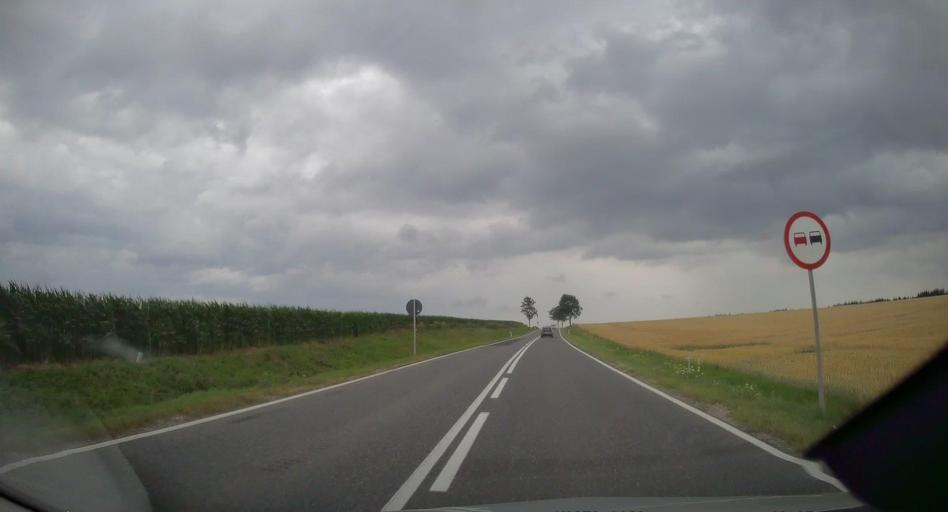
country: PL
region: Opole Voivodeship
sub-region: Powiat prudnicki
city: Moszczanka
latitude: 50.4205
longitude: 17.4674
